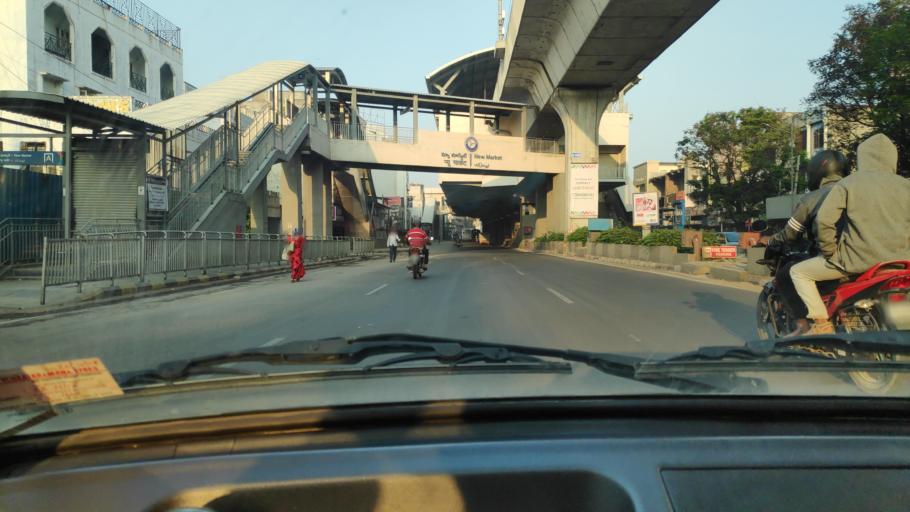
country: IN
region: Telangana
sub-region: Rangareddi
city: Gaddi Annaram
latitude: 17.3732
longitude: 78.5044
